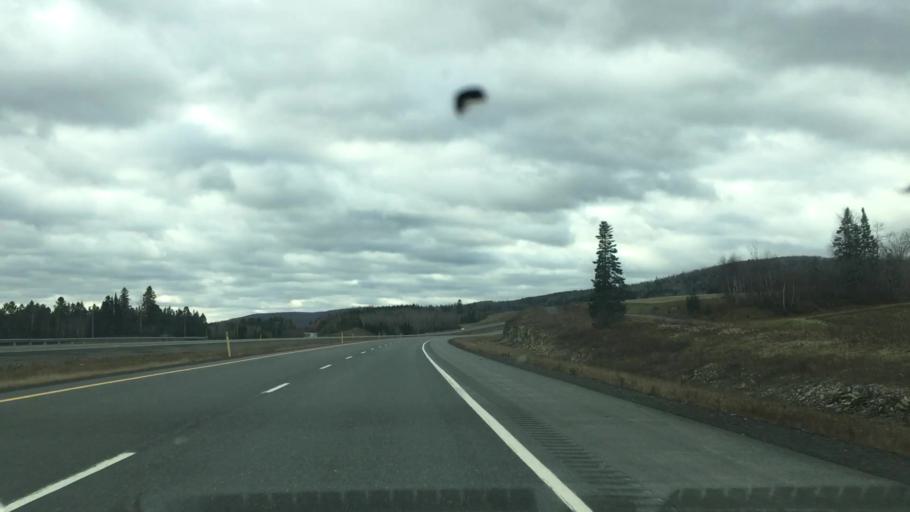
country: US
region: Maine
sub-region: Aroostook County
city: Fort Fairfield
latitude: 46.7370
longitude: -67.7177
